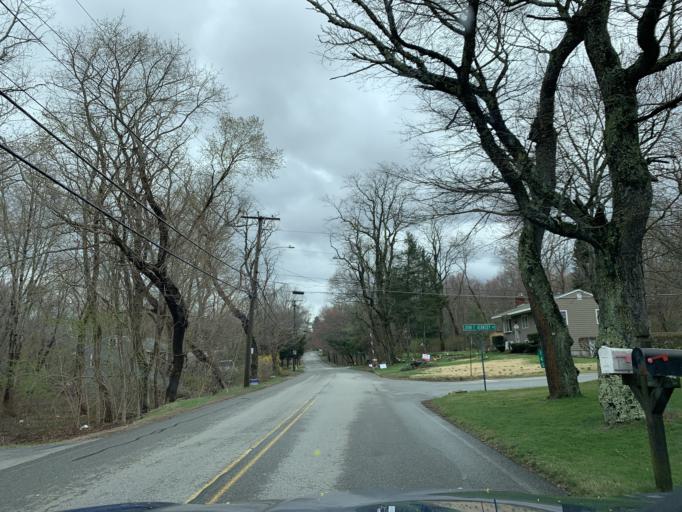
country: US
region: Massachusetts
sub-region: Bristol County
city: Attleboro
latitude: 41.9653
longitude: -71.2398
